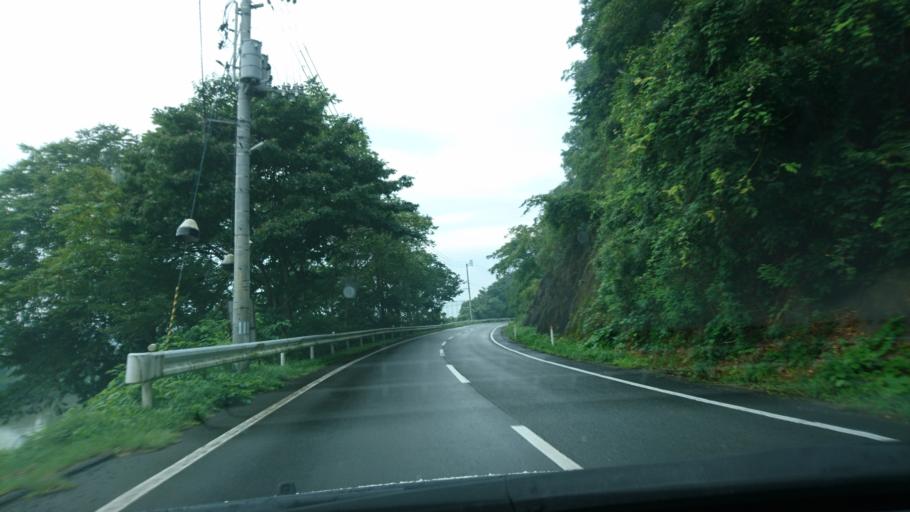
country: JP
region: Iwate
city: Ichinoseki
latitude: 38.8907
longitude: 141.2660
